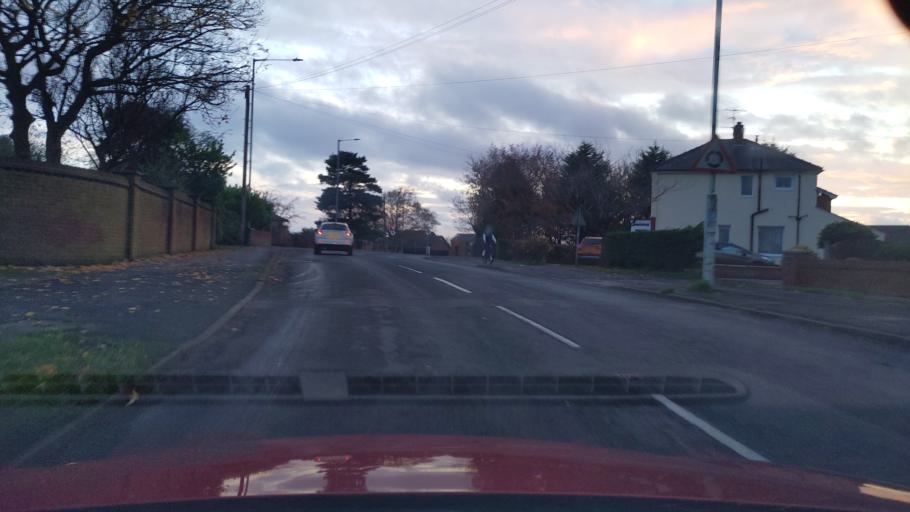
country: GB
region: England
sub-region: Lancashire
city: Clayton-le-Woods
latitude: 53.6988
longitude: -2.6603
